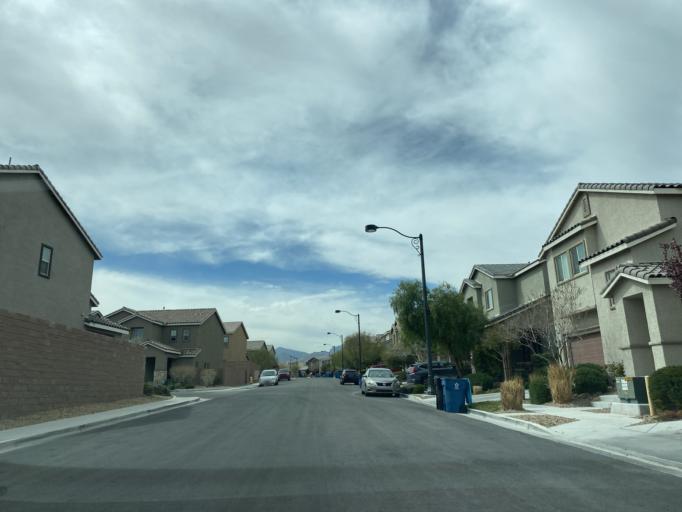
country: US
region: Nevada
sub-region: Clark County
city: Summerlin South
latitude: 36.3085
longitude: -115.2991
